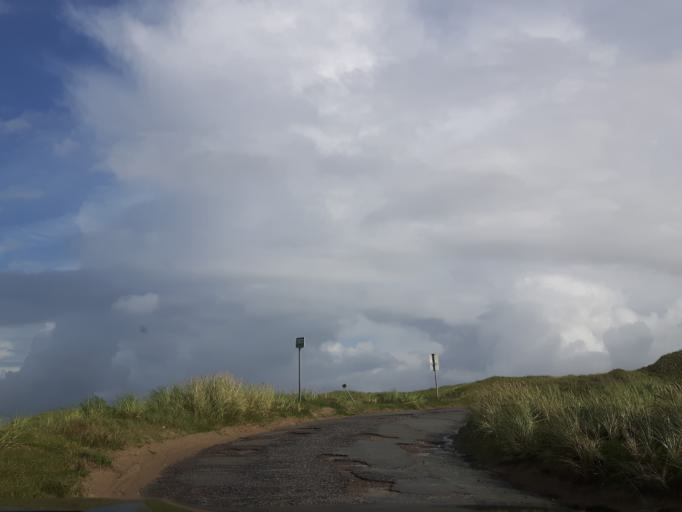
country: DK
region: North Denmark
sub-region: Thisted Kommune
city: Hanstholm
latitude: 57.0866
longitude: 8.5591
